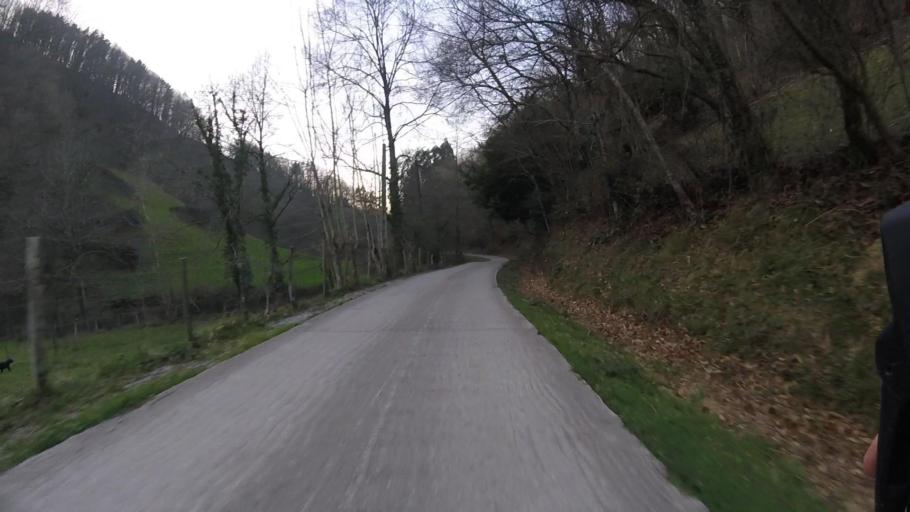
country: ES
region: Basque Country
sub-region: Provincia de Guipuzcoa
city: Errenteria
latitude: 43.2656
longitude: -1.8570
